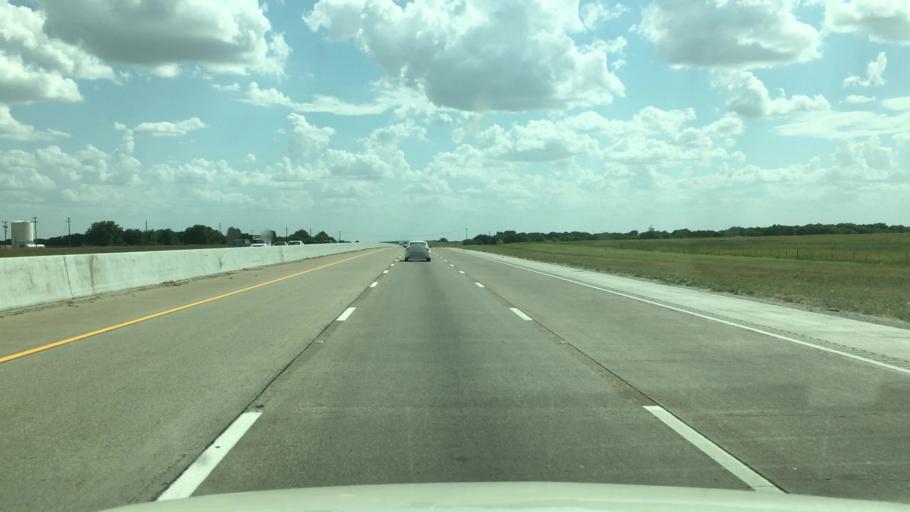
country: US
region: Texas
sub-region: Ellis County
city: Italy
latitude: 32.1635
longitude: -96.9204
